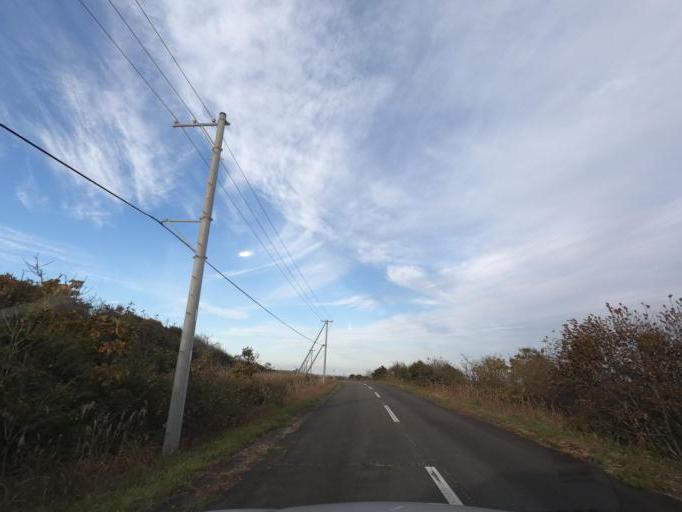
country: JP
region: Hokkaido
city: Obihiro
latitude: 42.5377
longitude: 143.4880
